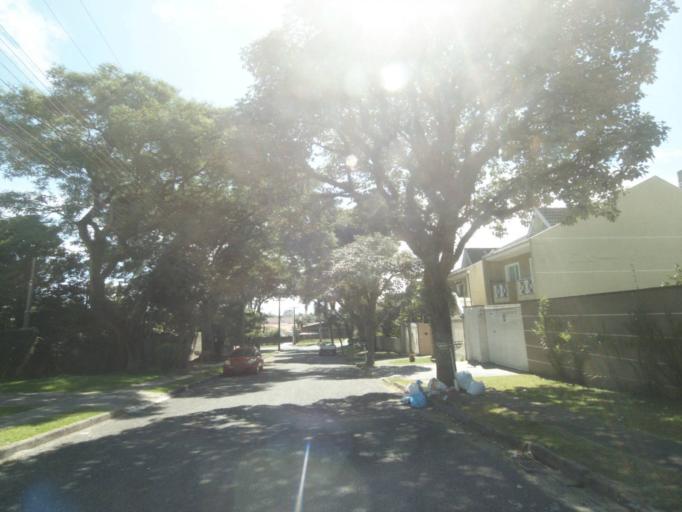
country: BR
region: Parana
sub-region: Curitiba
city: Curitiba
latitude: -25.4561
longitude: -49.2445
